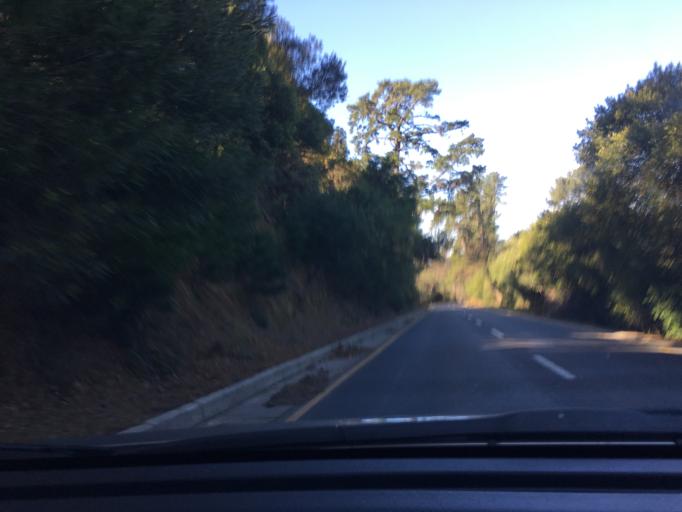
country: ZA
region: Western Cape
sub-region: City of Cape Town
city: Constantia
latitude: -34.0103
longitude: 18.4114
